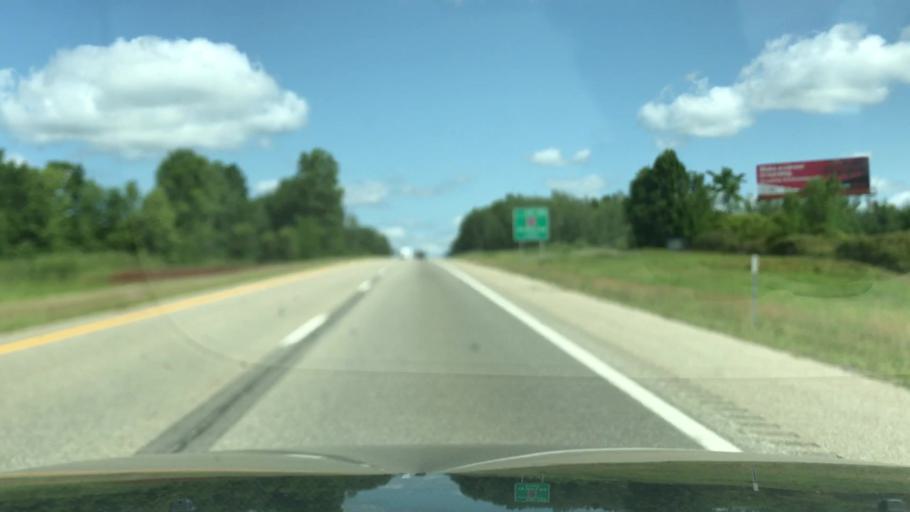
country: US
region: Michigan
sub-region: Mecosta County
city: Big Rapids
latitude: 43.7212
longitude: -85.5313
